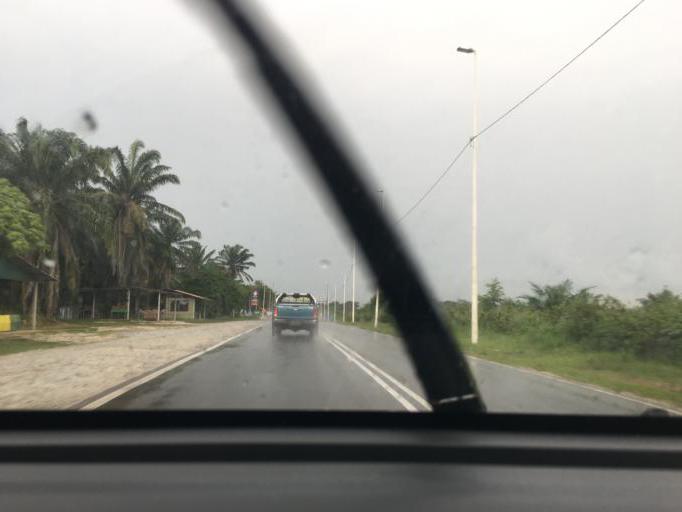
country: MY
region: Kedah
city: Sungai Petani
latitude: 5.5977
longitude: 100.6396
